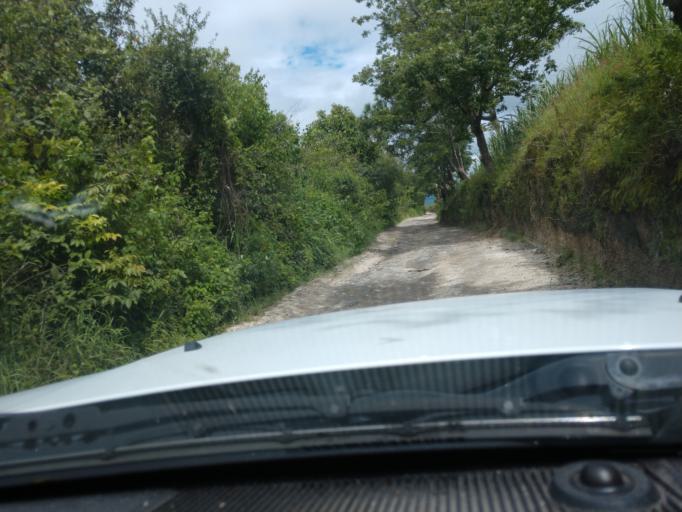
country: MX
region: Nayarit
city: Xalisco
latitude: 21.4386
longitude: -104.9201
